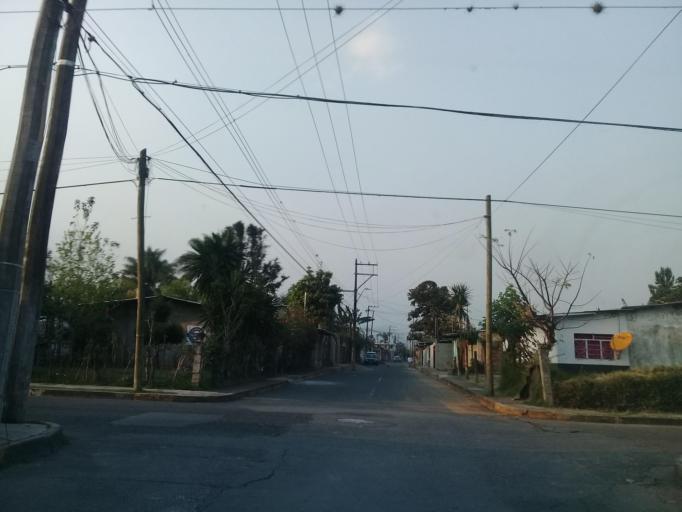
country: MX
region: Veracruz
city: Ixtac Zoquitlan
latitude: 18.8496
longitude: -97.0593
